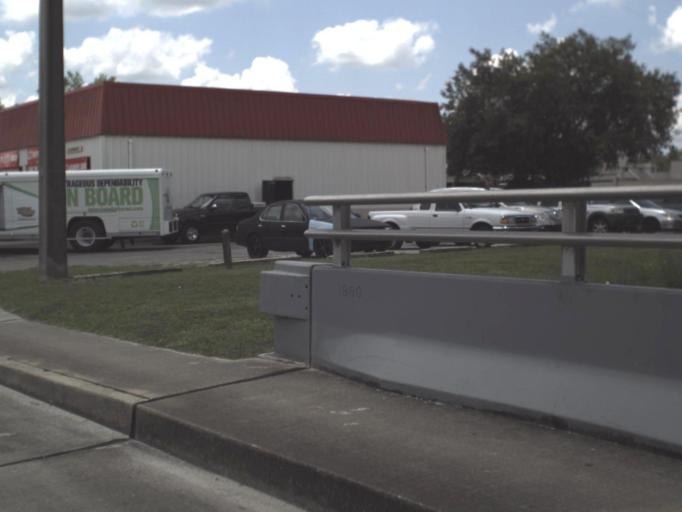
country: US
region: Florida
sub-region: Alachua County
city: Gainesville
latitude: 29.6528
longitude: -82.3725
